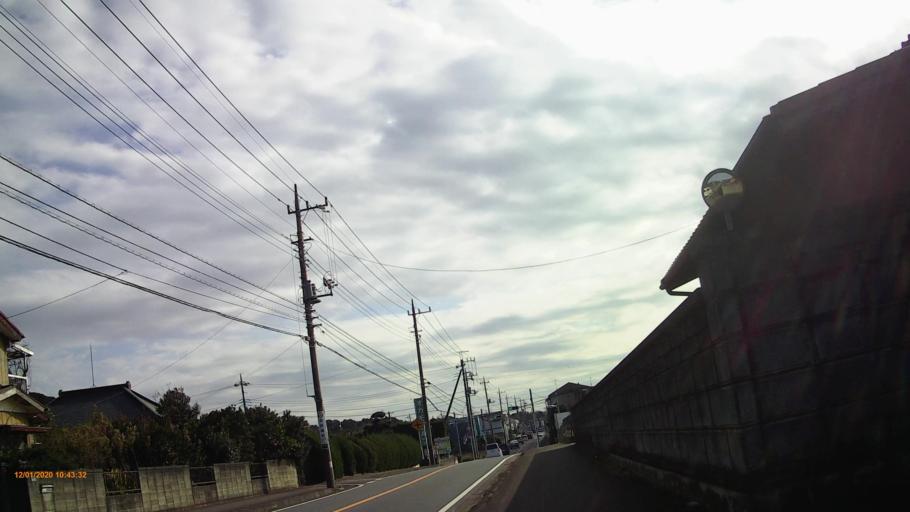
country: JP
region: Chiba
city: Yotsukaido
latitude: 35.6268
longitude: 140.1911
